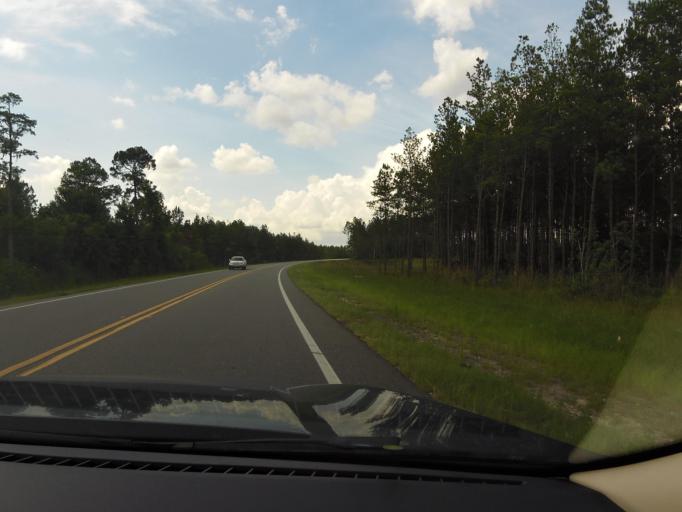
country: US
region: Florida
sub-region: Baker County
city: Macclenny
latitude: 30.2200
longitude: -82.0746
